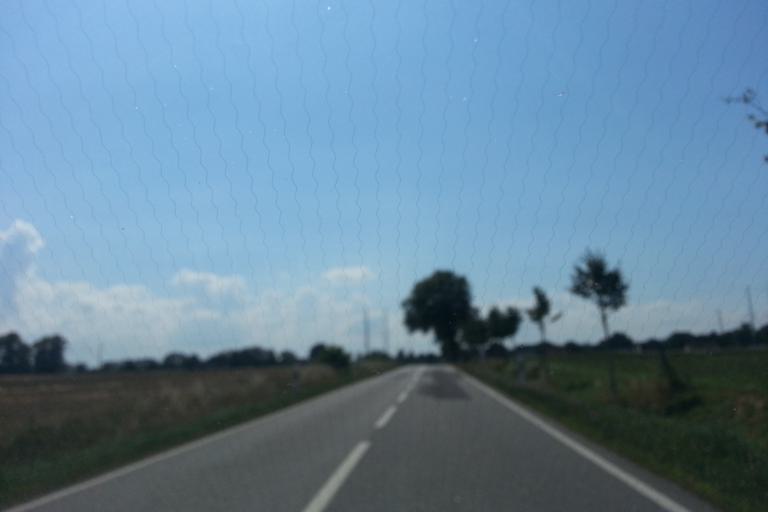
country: DE
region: Mecklenburg-Vorpommern
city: Ferdinandshof
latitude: 53.7072
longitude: 13.8440
